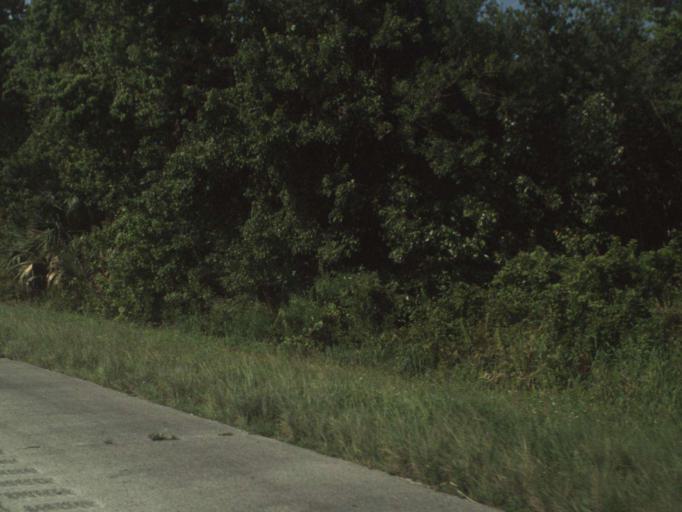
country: US
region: Florida
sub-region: Indian River County
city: Fellsmere
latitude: 27.7525
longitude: -80.5514
